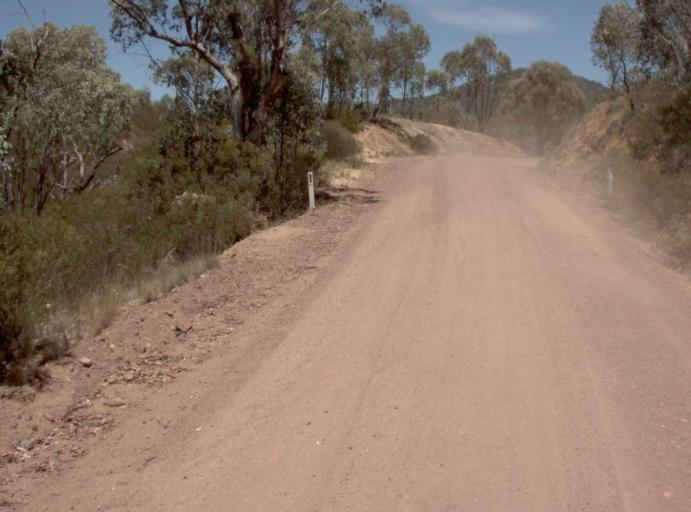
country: AU
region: New South Wales
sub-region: Snowy River
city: Jindabyne
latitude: -36.9214
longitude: 148.3966
